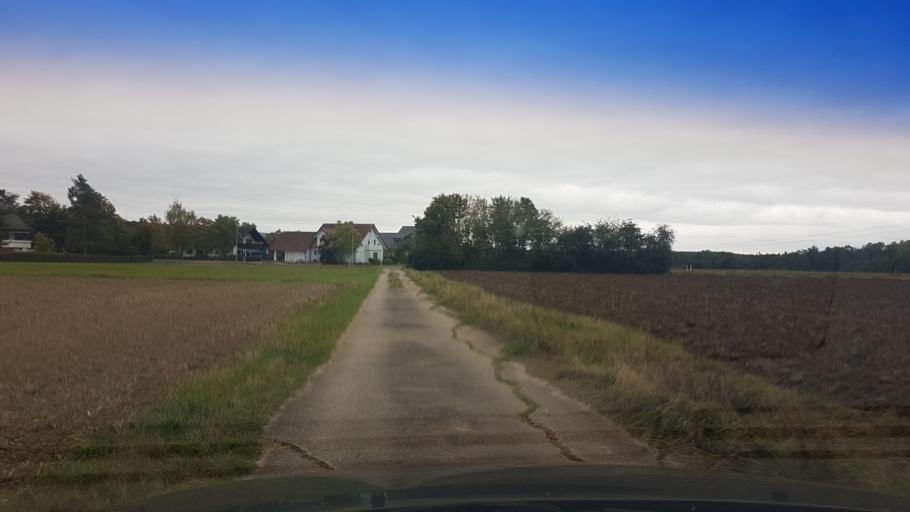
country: DE
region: Bavaria
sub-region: Upper Franconia
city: Memmelsdorf
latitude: 49.9343
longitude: 10.9765
